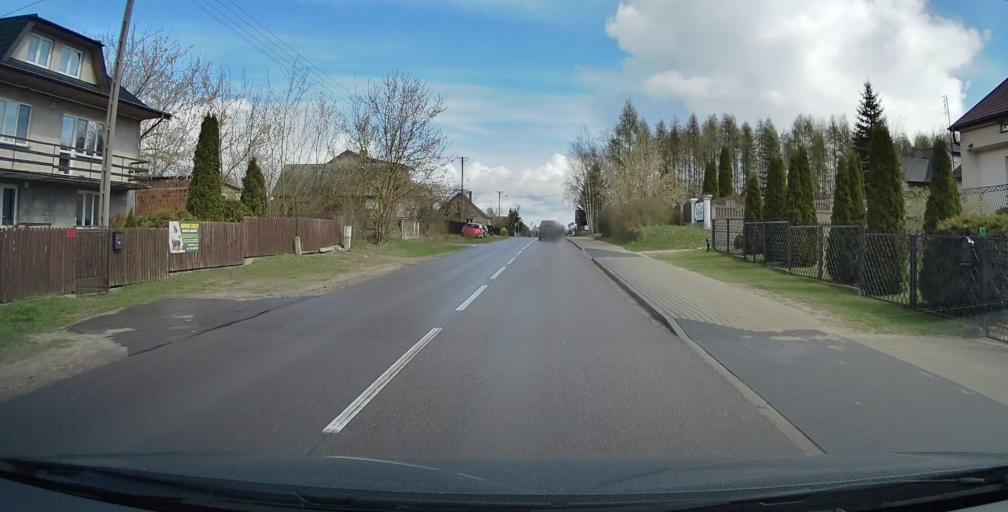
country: PL
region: Masovian Voivodeship
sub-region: Powiat wyszkowski
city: Branszczyk
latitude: 52.6875
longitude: 21.5926
